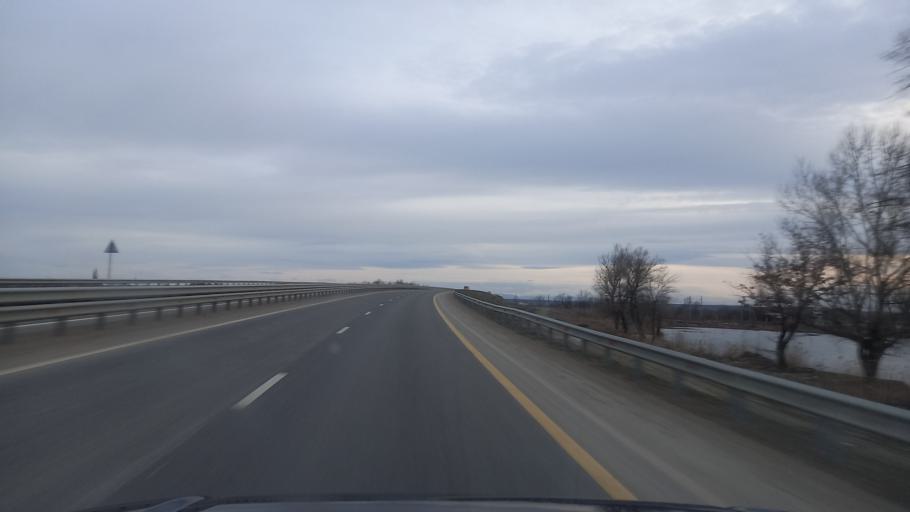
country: RU
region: Adygeya
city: Khanskaya
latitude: 44.7040
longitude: 39.9681
